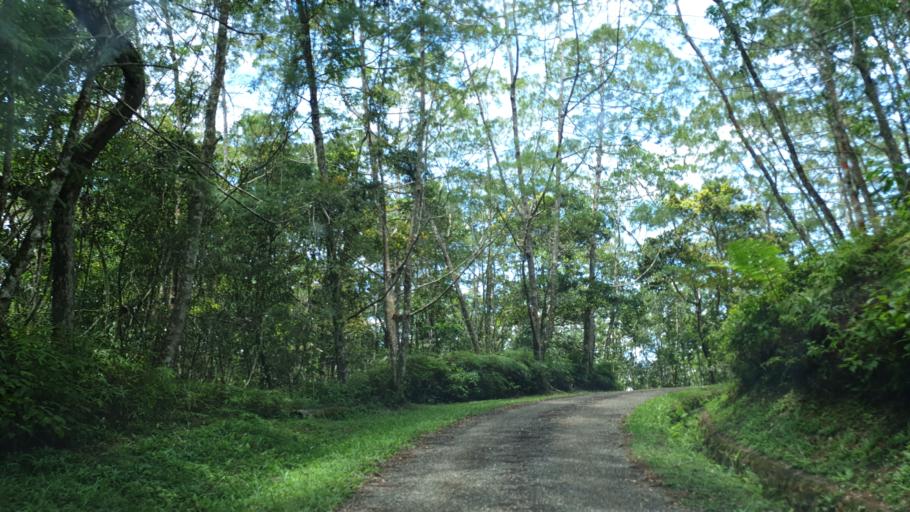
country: PG
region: National Capital
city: Port Moresby
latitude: -9.4352
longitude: 147.3650
